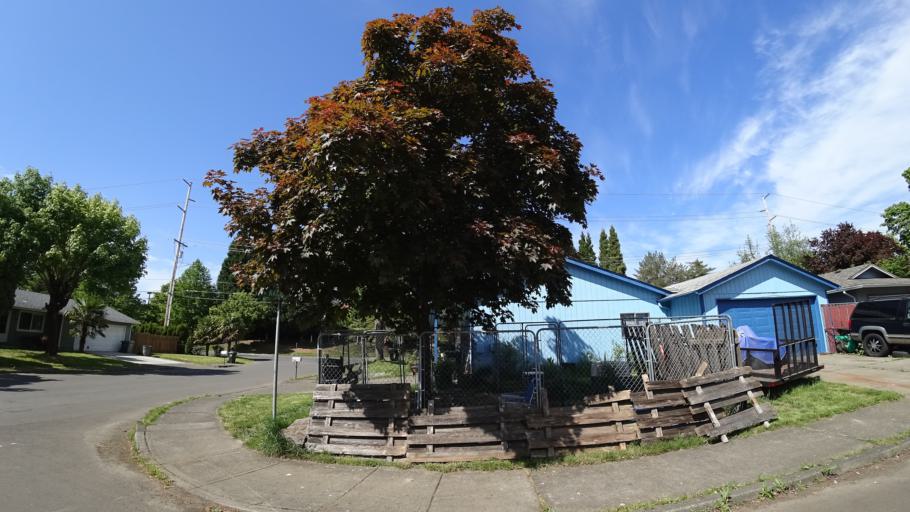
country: US
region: Oregon
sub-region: Washington County
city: Aloha
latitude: 45.4917
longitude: -122.8852
